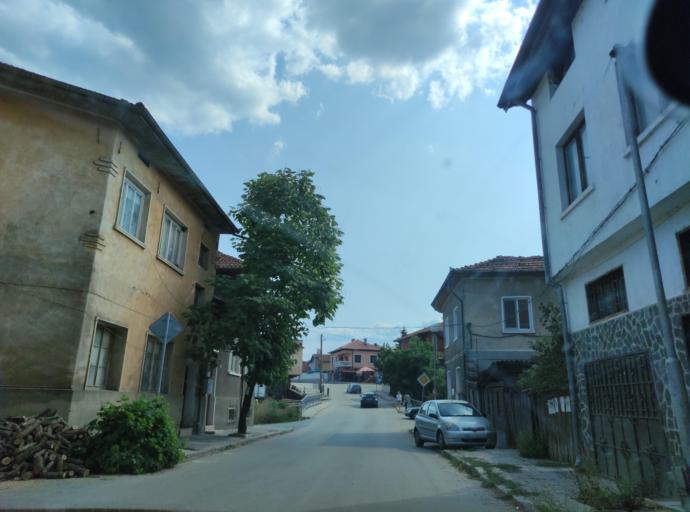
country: BG
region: Blagoevgrad
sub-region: Obshtina Belitsa
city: Belitsa
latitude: 41.9503
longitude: 23.5556
